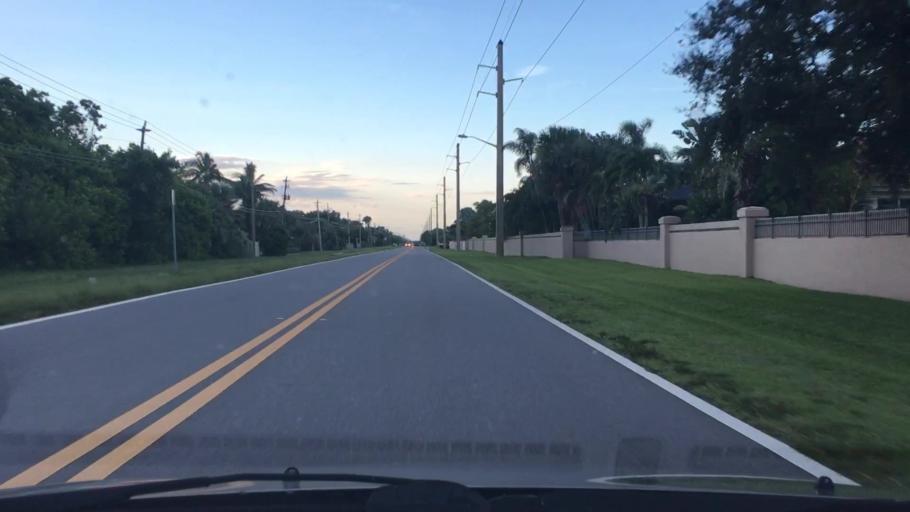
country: US
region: Florida
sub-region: Brevard County
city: Indialantic
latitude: 28.1091
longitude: -80.5835
